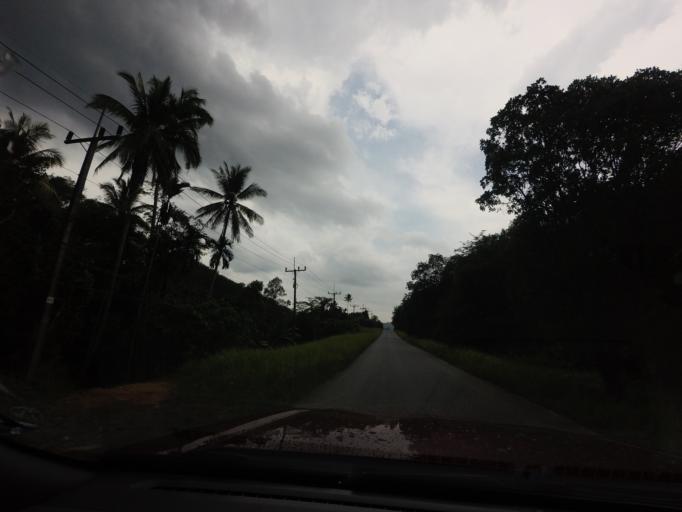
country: TH
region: Yala
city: Ban Nang Sata
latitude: 6.2191
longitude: 101.2306
